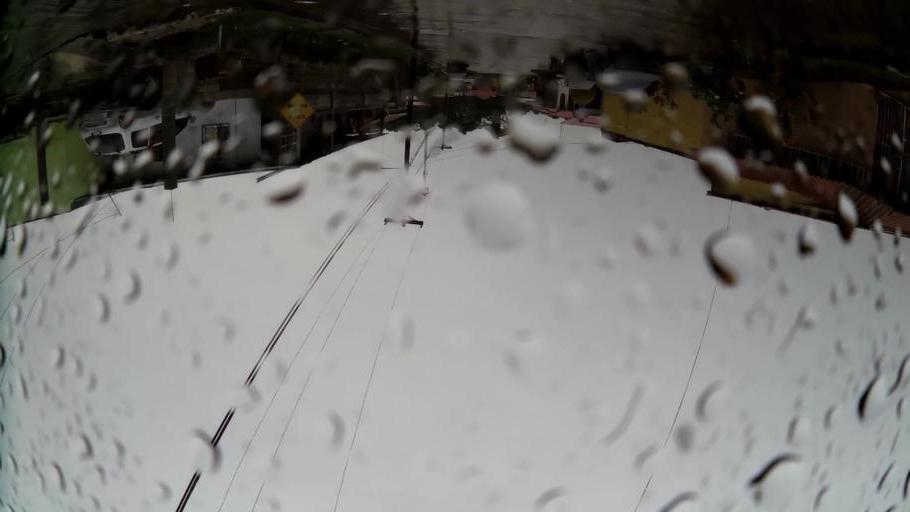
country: PA
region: Colon
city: Puerto Pilon
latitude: 9.3567
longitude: -79.7898
